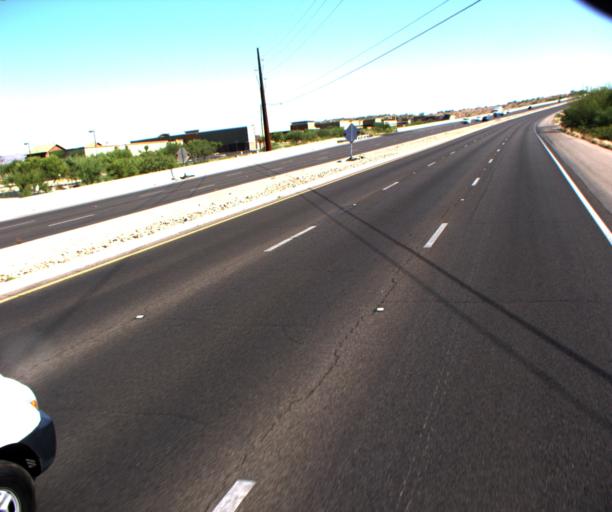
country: US
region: Arizona
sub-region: Pima County
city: Oro Valley
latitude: 32.4193
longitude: -110.9371
